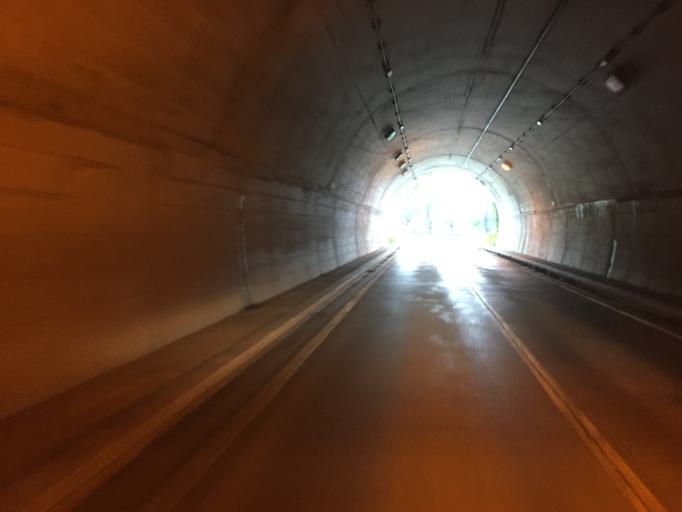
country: JP
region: Fukushima
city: Inawashiro
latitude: 37.4606
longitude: 139.9679
